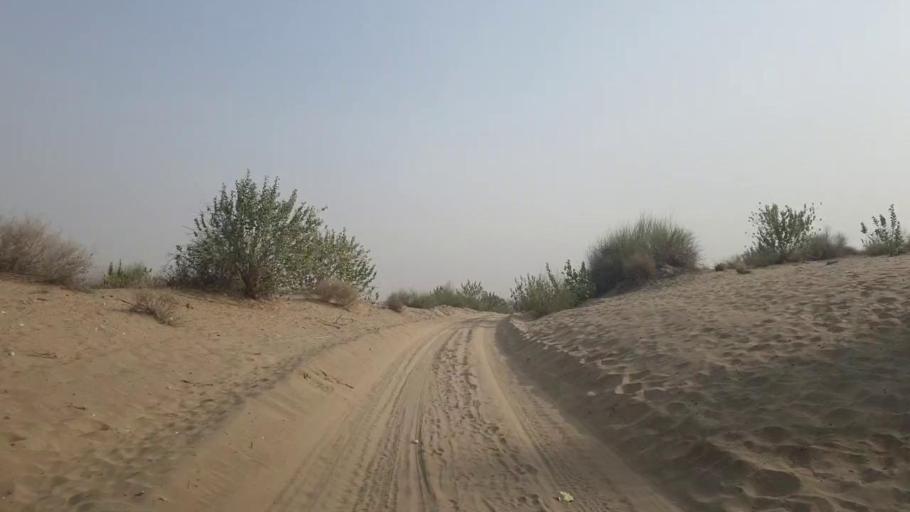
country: PK
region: Sindh
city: Chor
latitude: 25.4475
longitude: 69.9642
